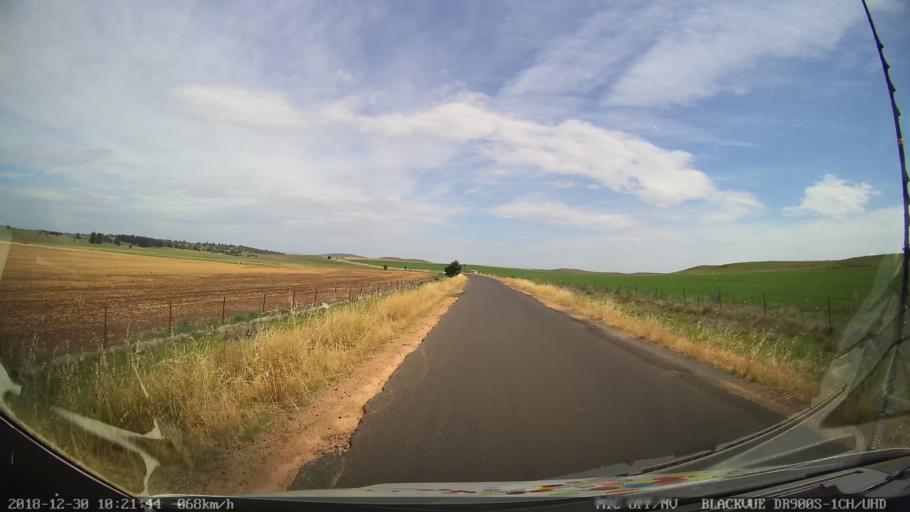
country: AU
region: New South Wales
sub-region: Snowy River
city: Berridale
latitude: -36.5494
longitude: 149.0027
